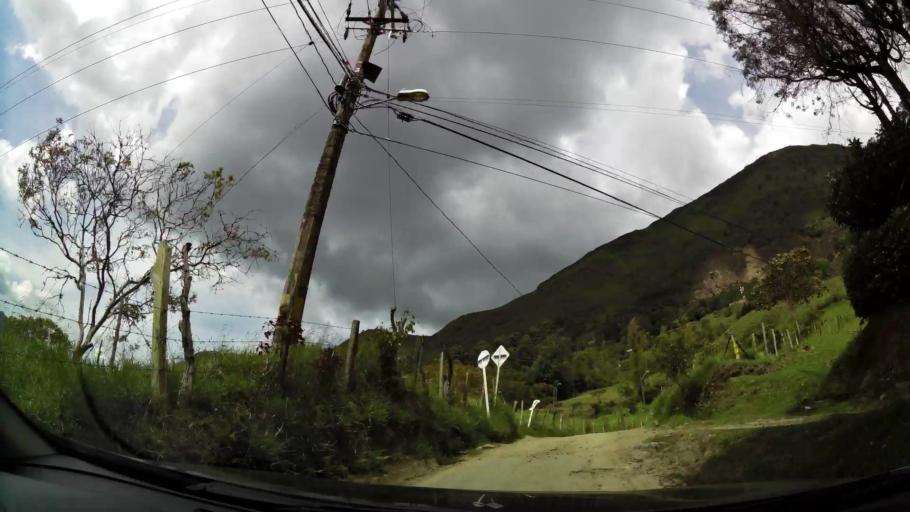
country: CO
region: Antioquia
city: Municipio de Copacabana
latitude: 6.3223
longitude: -75.4936
